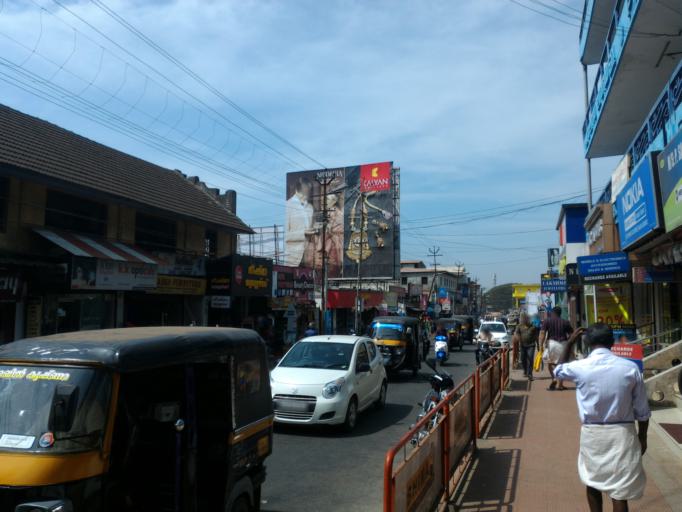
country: IN
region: Kerala
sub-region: Palakkad district
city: Palakkad
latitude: 10.7734
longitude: 76.6567
